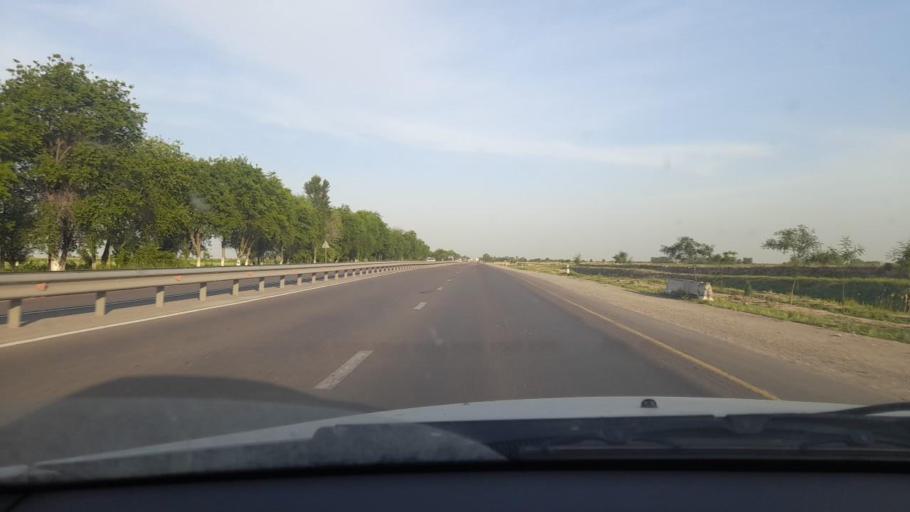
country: KZ
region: Ongtustik Qazaqstan
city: Myrzakent
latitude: 40.5323
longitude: 68.4358
